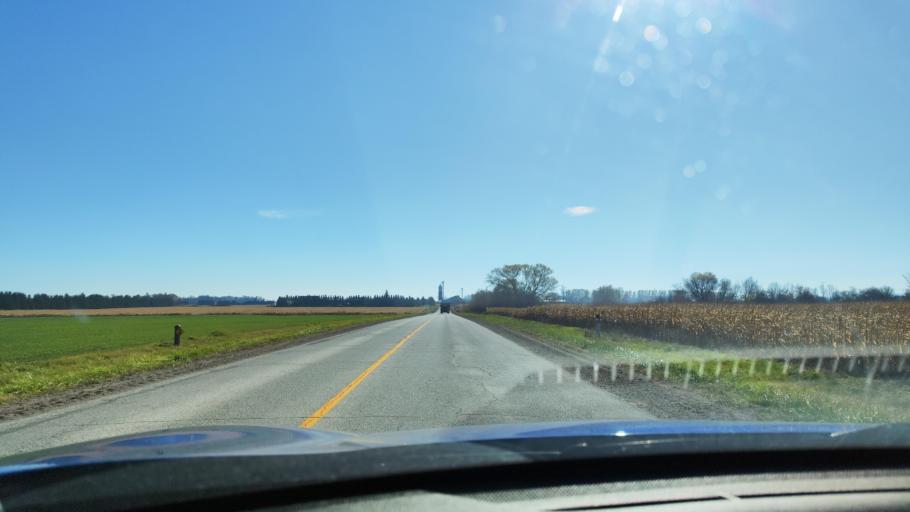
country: CA
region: Ontario
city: Wasaga Beach
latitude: 44.4483
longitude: -80.0005
